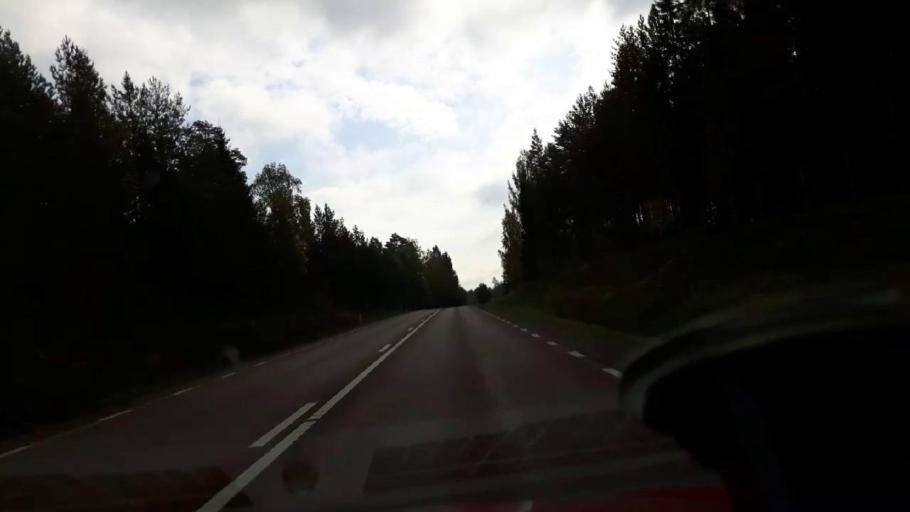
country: SE
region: Gaevleborg
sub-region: Bollnas Kommun
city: Kilafors
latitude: 61.2648
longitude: 16.5485
